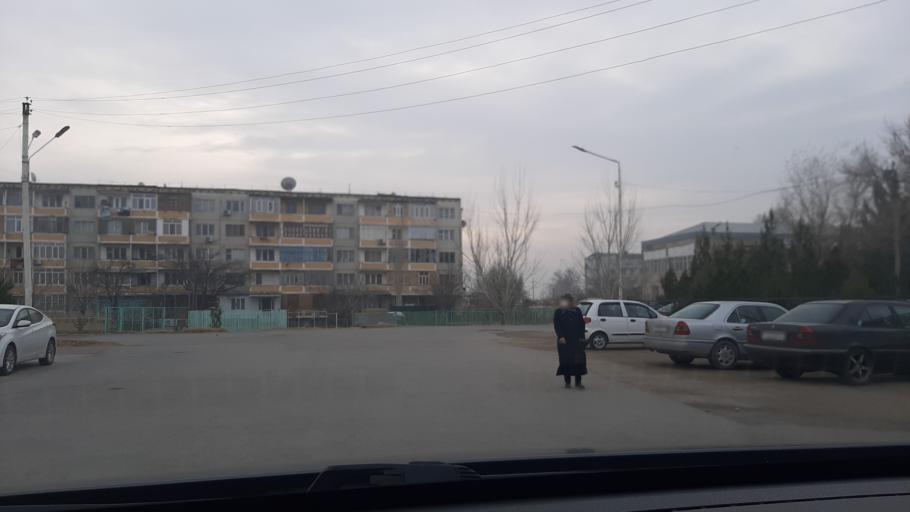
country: TJ
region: Viloyati Sughd
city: Palos
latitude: 40.2611
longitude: 69.7932
